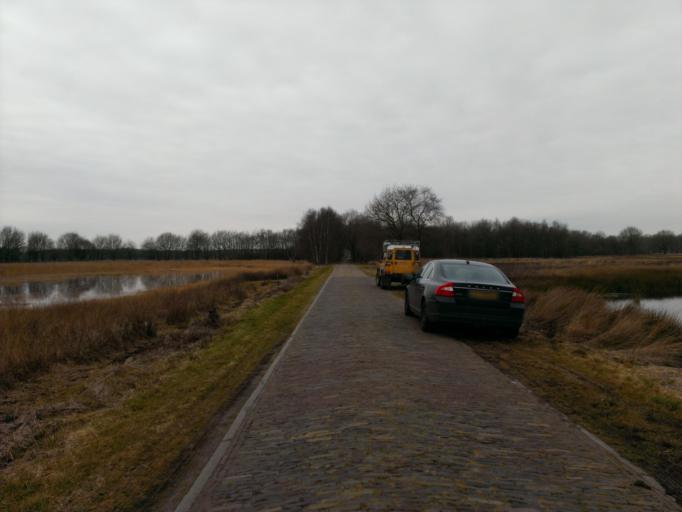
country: NL
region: Drenthe
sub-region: Gemeente Hoogeveen
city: Hoogeveen
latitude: 52.7595
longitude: 6.4783
